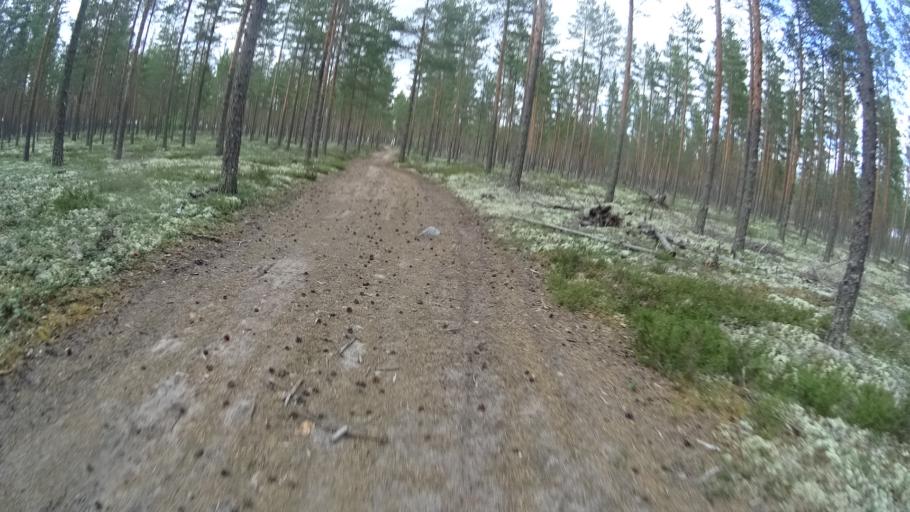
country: FI
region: Satakunta
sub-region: Pohjois-Satakunta
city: Jaemijaervi
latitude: 61.7679
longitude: 22.8023
